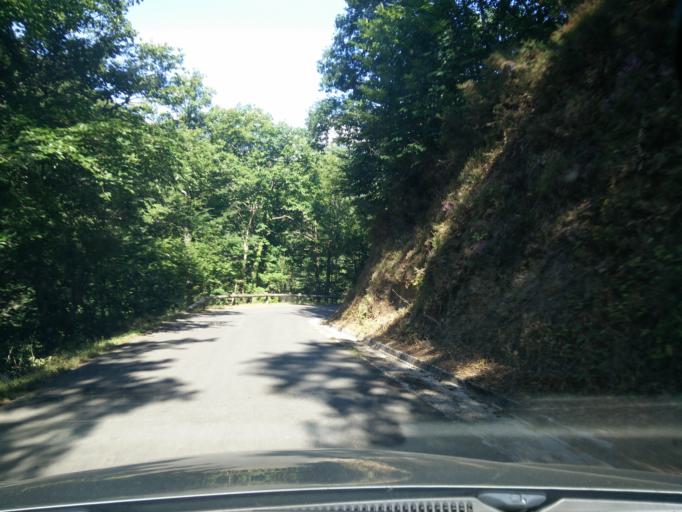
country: ES
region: Asturias
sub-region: Province of Asturias
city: Campo de Caso
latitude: 43.1518
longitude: -5.3868
